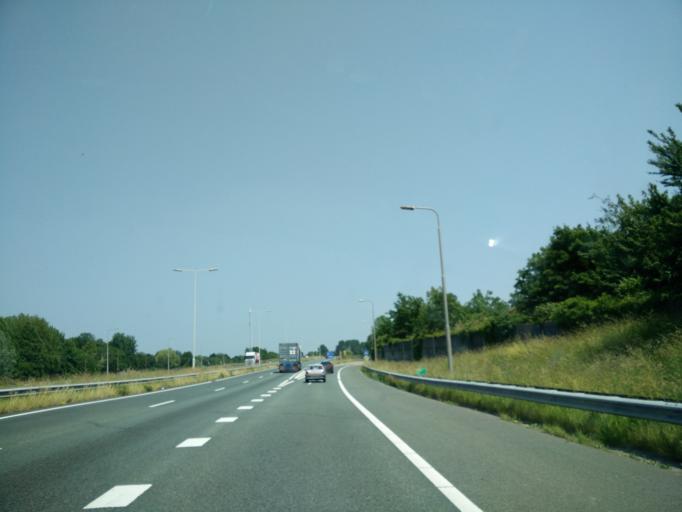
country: NL
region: South Holland
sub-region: Gemeente Dordrecht
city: Dordrecht
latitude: 51.7810
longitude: 4.6645
